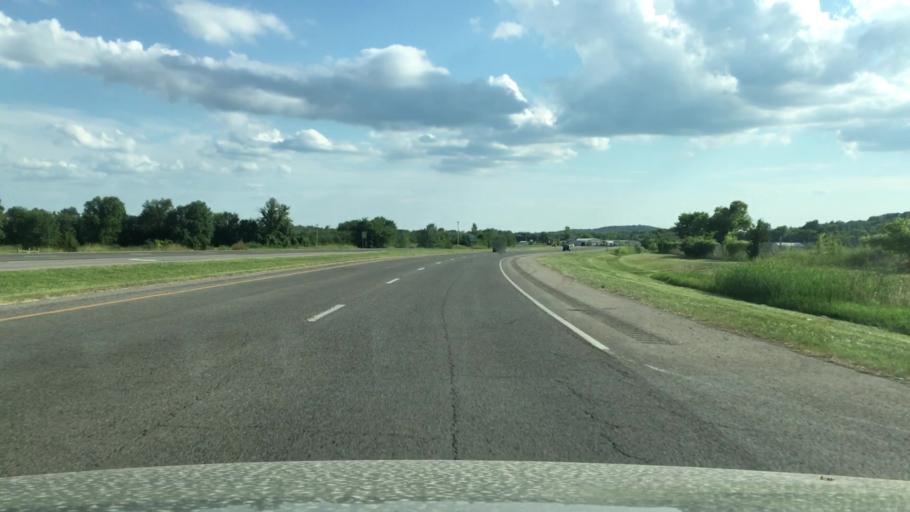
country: US
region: Oklahoma
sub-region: Cherokee County
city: Tahlequah
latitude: 35.9255
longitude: -95.0014
